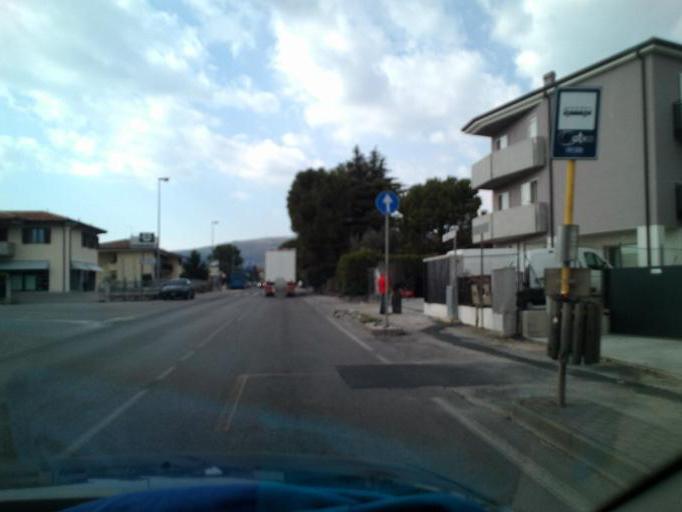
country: IT
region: Veneto
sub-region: Provincia di Verona
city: San Pietro in Cariano
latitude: 45.5173
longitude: 10.8918
